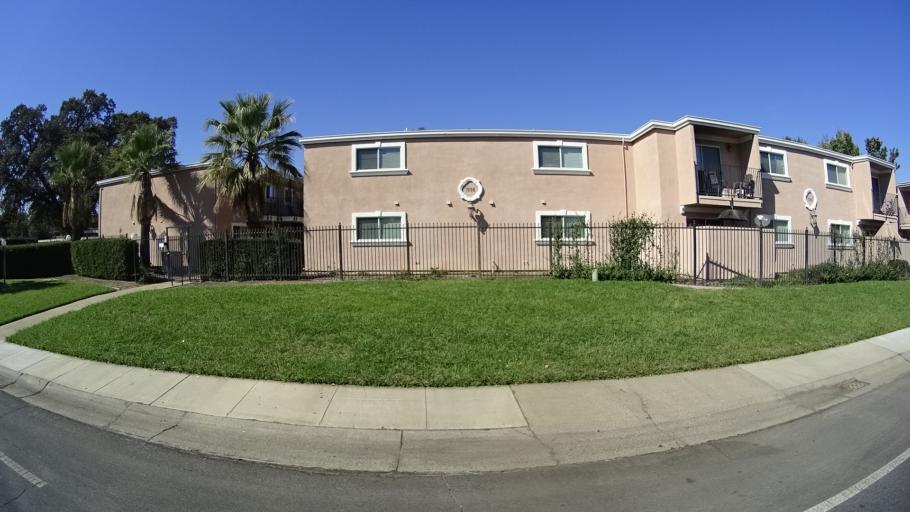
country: US
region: California
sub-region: Sacramento County
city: Parkway
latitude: 38.4965
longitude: -121.5118
